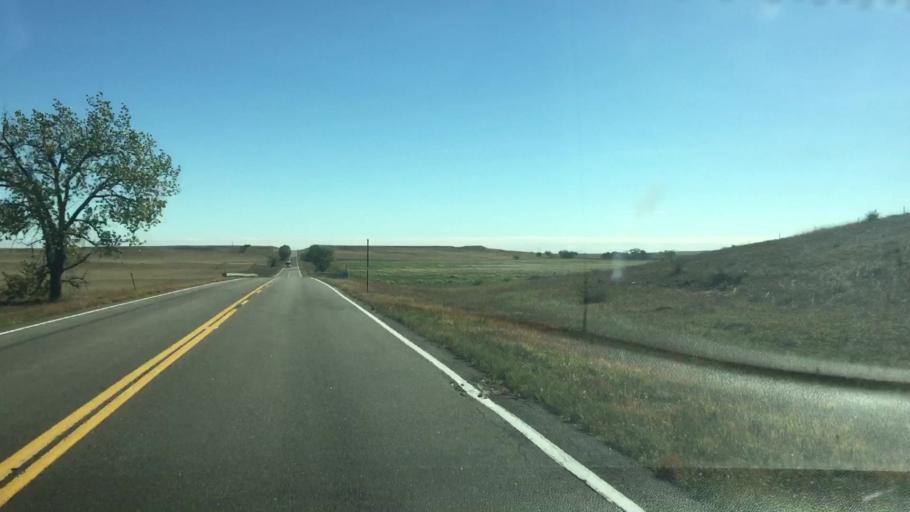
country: US
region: Colorado
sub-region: Lincoln County
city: Limon
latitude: 39.2947
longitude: -103.8965
